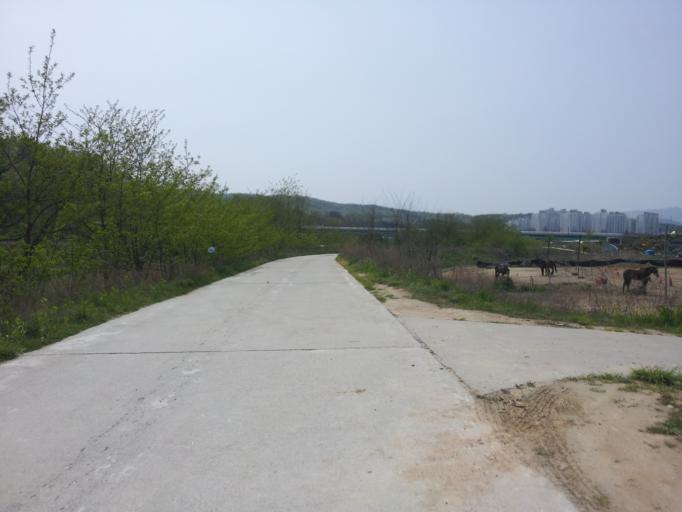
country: KR
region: Daejeon
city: Daejeon
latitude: 36.2653
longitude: 127.2836
